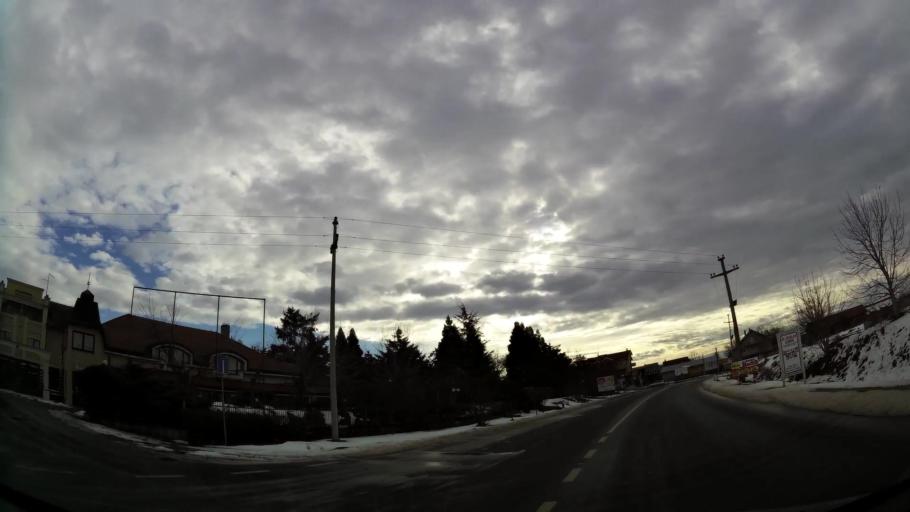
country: RS
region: Central Serbia
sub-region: Belgrade
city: Surcin
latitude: 44.7997
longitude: 20.3203
